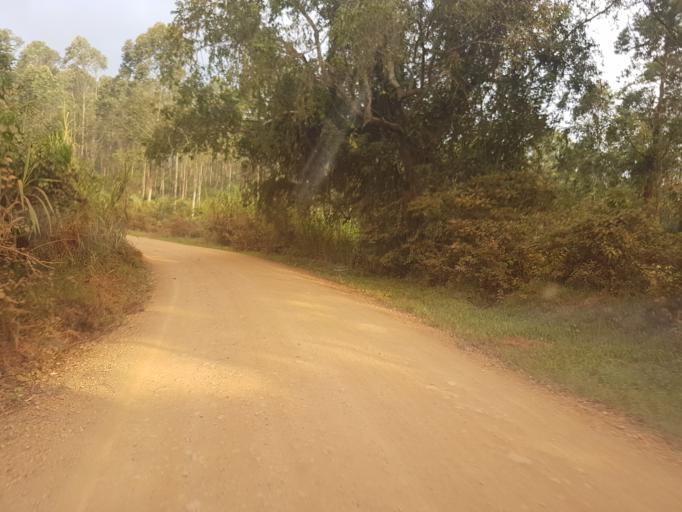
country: UG
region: Western Region
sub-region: Rukungiri District
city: Rukungiri
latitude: -0.6645
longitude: 29.8647
